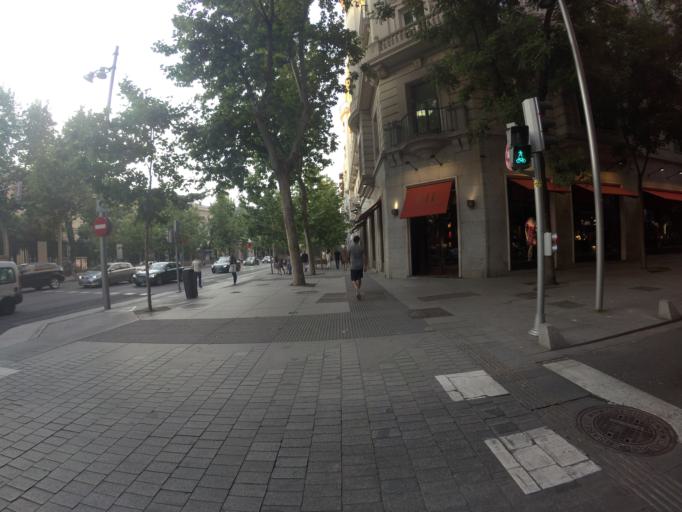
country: ES
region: Madrid
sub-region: Provincia de Madrid
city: Retiro
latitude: 40.4226
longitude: -3.6882
